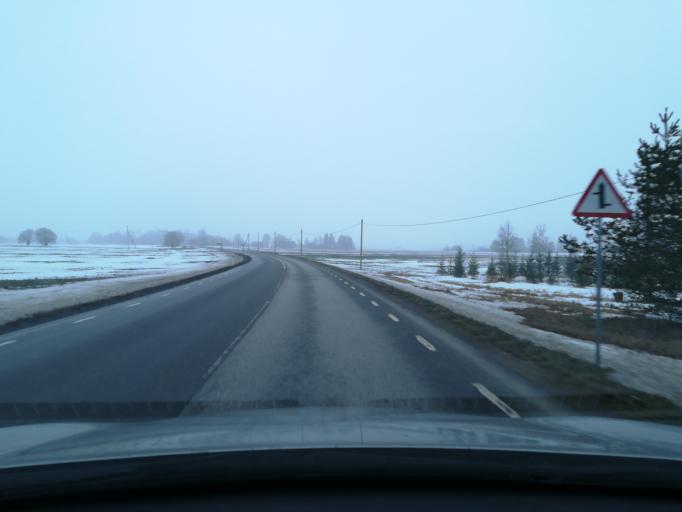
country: EE
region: Harju
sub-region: Raasiku vald
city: Raasiku
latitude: 59.3550
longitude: 25.1459
